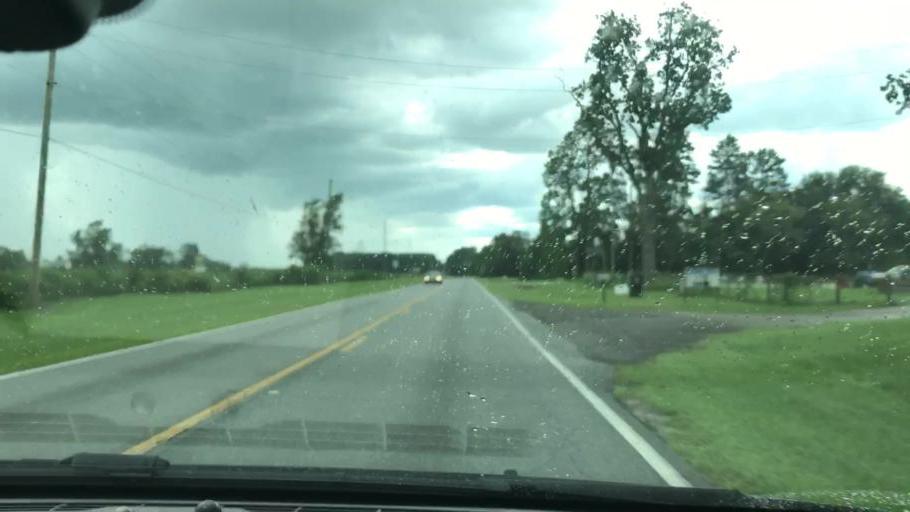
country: US
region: Florida
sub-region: Madison County
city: Madison
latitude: 30.4117
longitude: -83.3002
